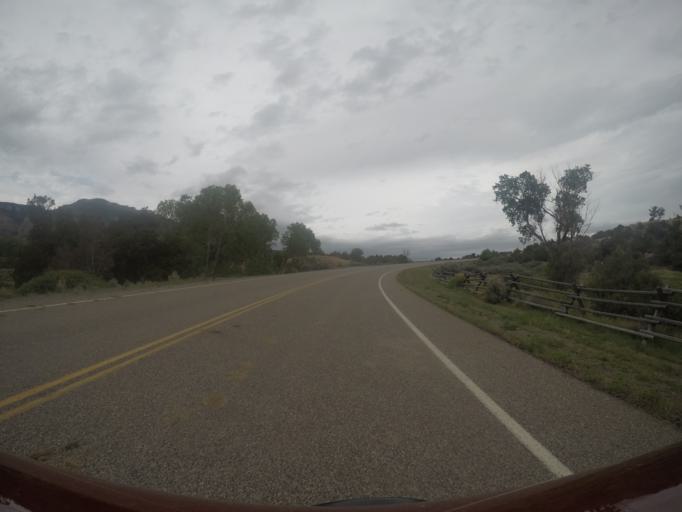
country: US
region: Wyoming
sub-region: Big Horn County
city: Lovell
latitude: 45.0823
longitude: -108.2612
